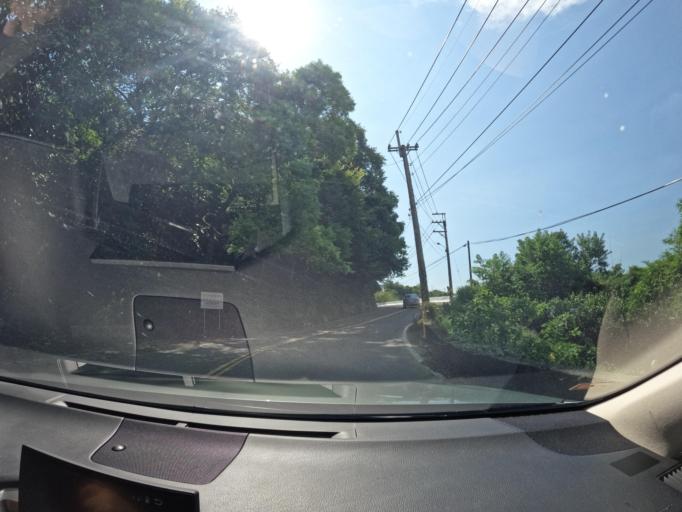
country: TW
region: Taiwan
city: Fengyuan
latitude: 24.3147
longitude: 120.7721
